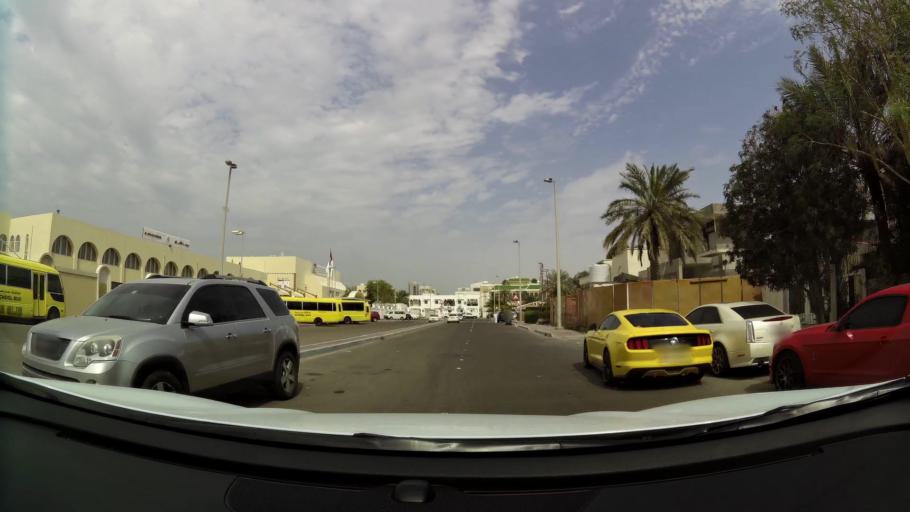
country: AE
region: Abu Dhabi
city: Abu Dhabi
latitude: 24.4585
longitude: 54.3683
